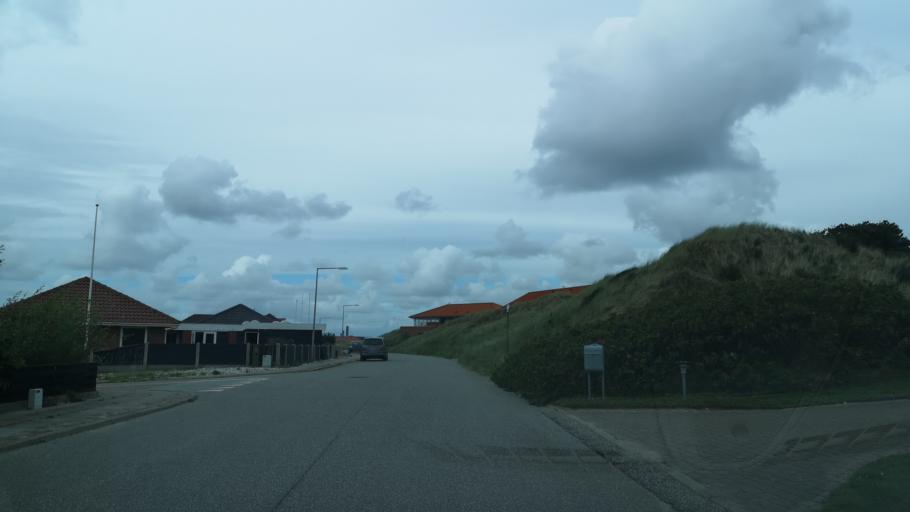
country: DK
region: Central Jutland
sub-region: Ringkobing-Skjern Kommune
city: Hvide Sande
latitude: 55.9947
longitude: 8.1316
